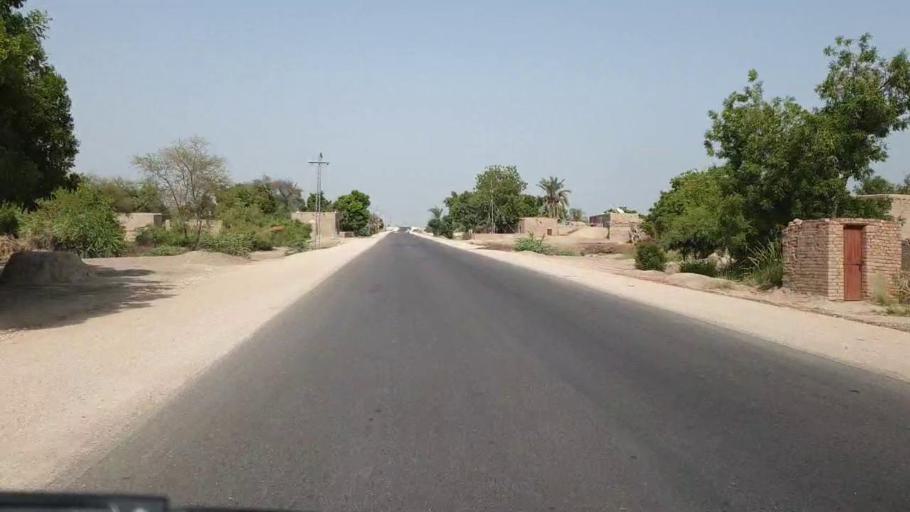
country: PK
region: Sindh
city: Sakrand
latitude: 26.2449
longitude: 68.2547
